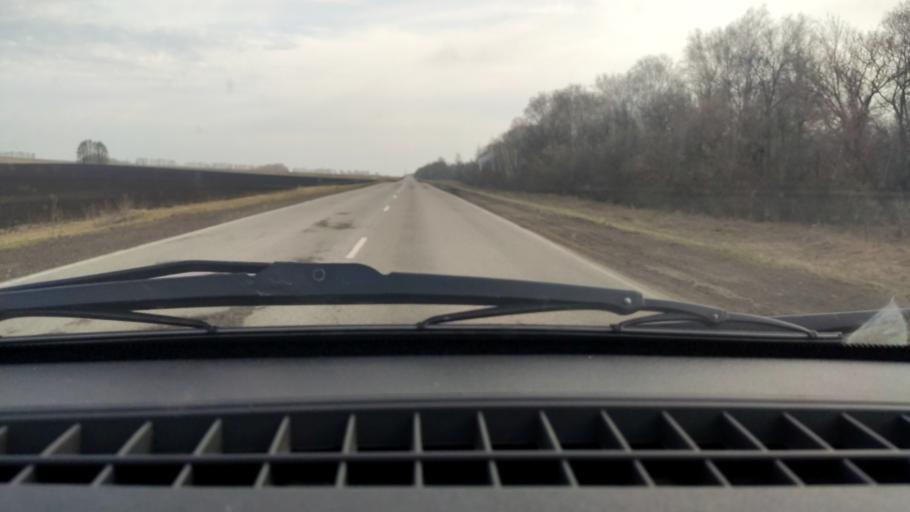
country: RU
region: Bashkortostan
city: Chishmy
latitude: 54.4642
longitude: 55.2576
